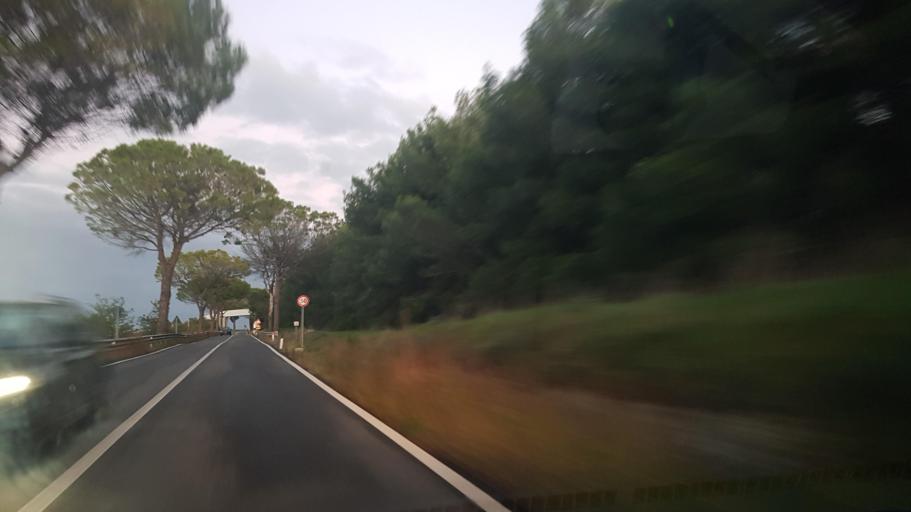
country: IT
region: Basilicate
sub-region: Provincia di Matera
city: Matera
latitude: 40.6768
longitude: 16.6709
